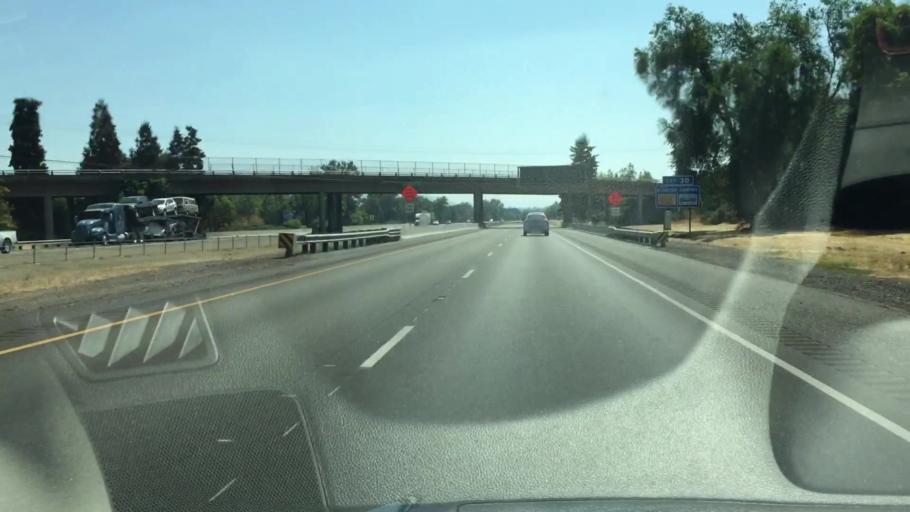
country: US
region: Oregon
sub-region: Jackson County
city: Central Point
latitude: 42.3639
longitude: -122.8865
